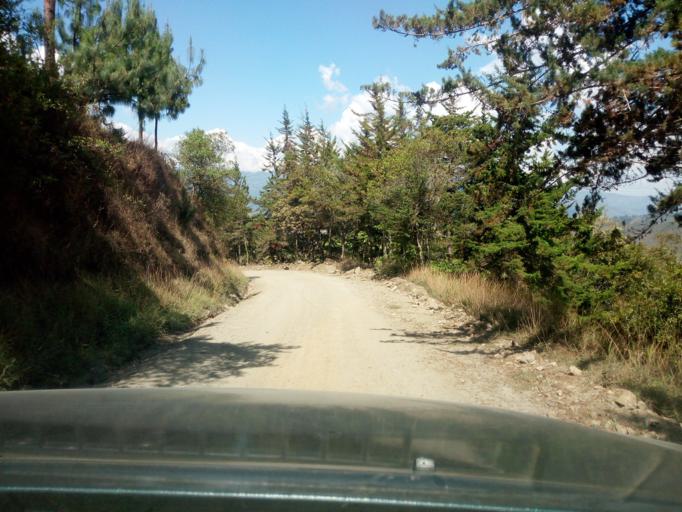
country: CO
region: Boyaca
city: Somondoco
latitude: 4.9771
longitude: -73.4041
